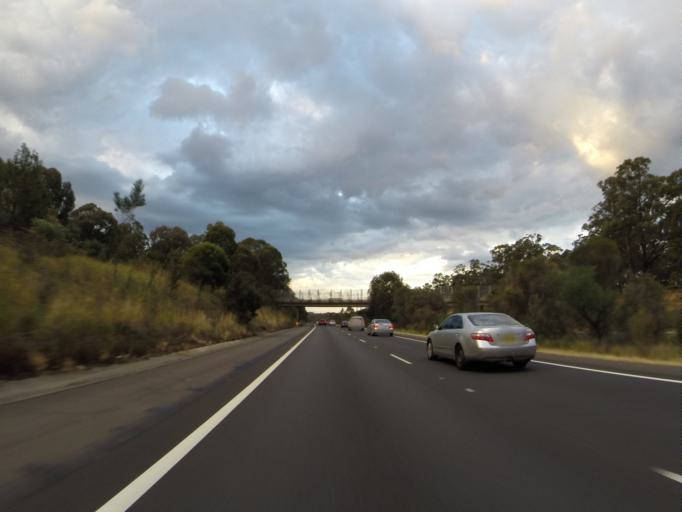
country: AU
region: New South Wales
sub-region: Wollondilly
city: Douglas Park
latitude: -34.1979
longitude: 150.7068
